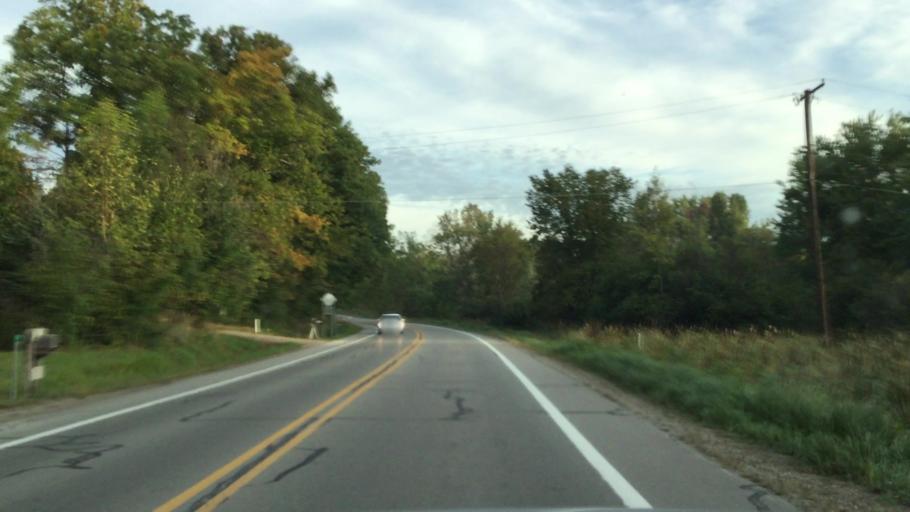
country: US
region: Michigan
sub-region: Livingston County
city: Whitmore Lake
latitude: 42.4451
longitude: -83.7828
